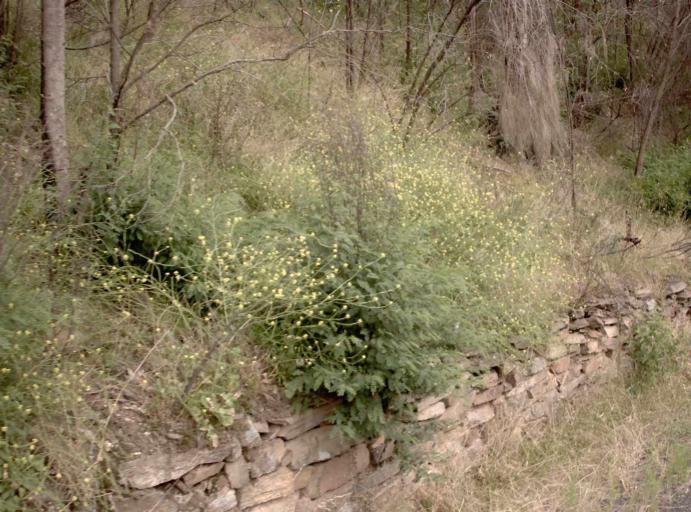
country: AU
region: Victoria
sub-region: Wellington
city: Heyfield
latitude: -37.7714
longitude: 146.6664
